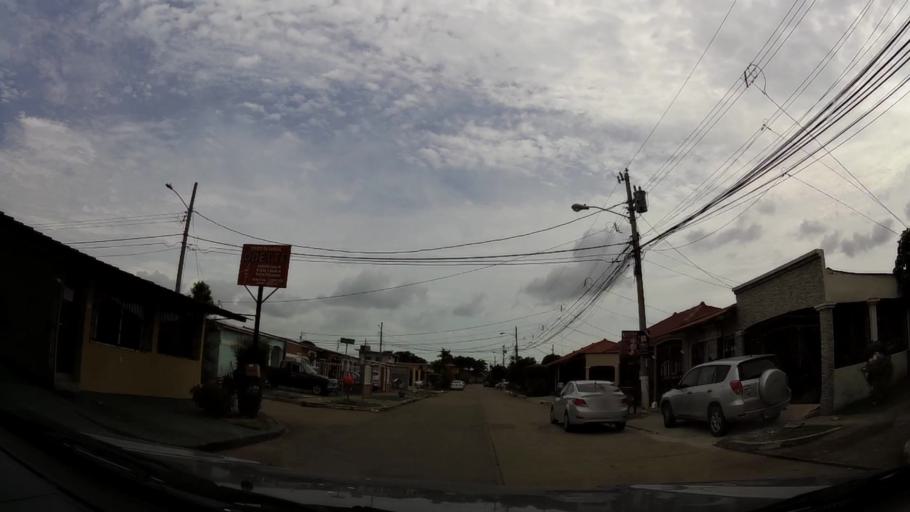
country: PA
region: Panama
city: Tocumen
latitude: 9.0424
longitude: -79.4082
